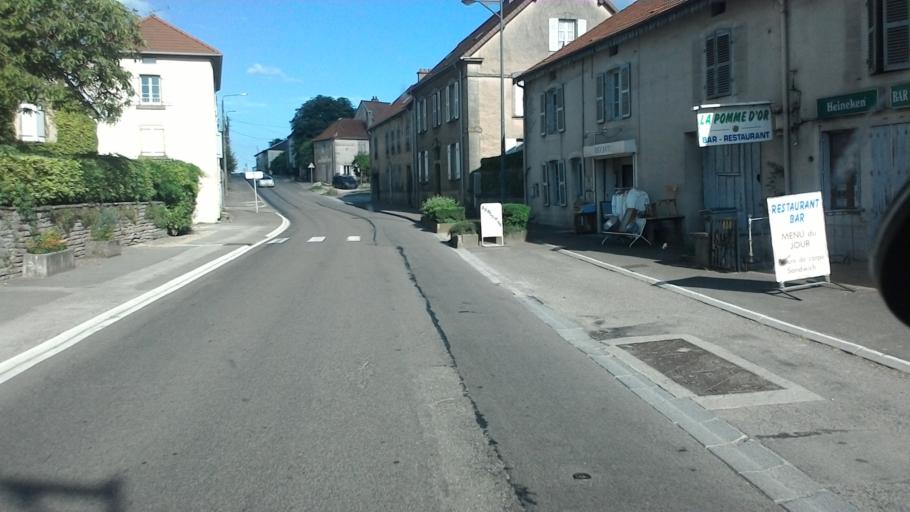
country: FR
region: Franche-Comte
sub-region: Departement de la Haute-Saone
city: Frotey-les-Vesoul
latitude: 47.6955
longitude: 6.2806
